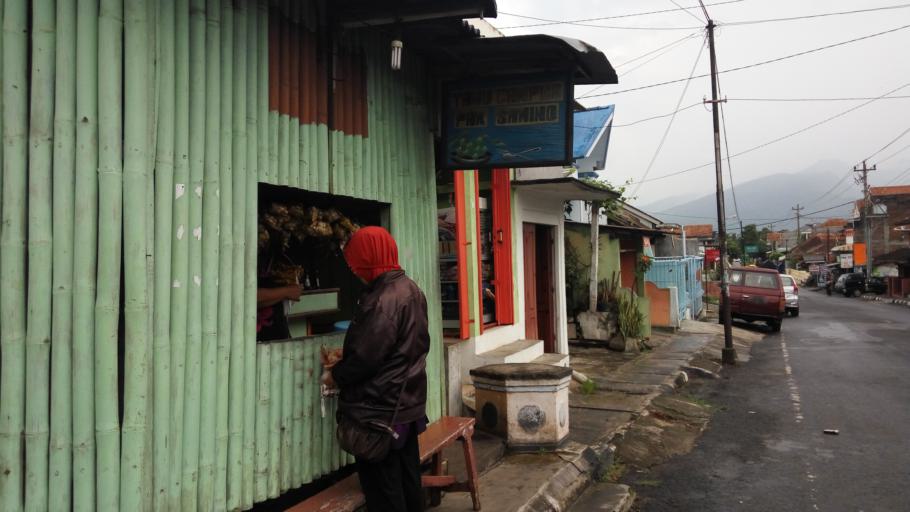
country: ID
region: Central Java
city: Ambarawa
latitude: -7.2619
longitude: 110.4061
